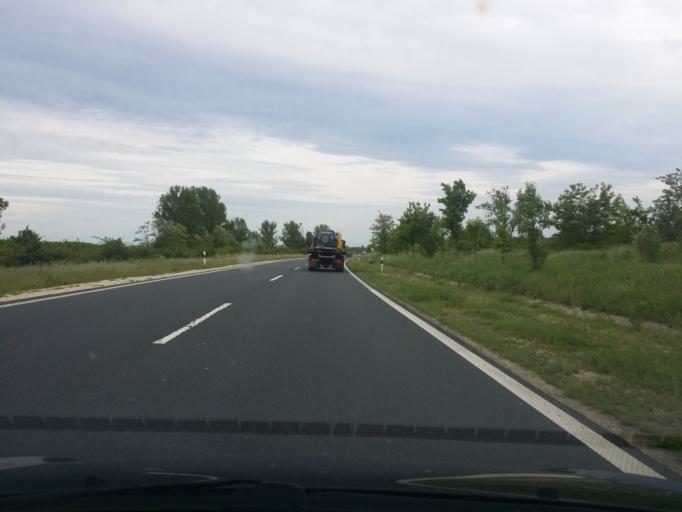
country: HU
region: Fejer
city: Lepseny
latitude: 47.0227
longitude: 18.1820
